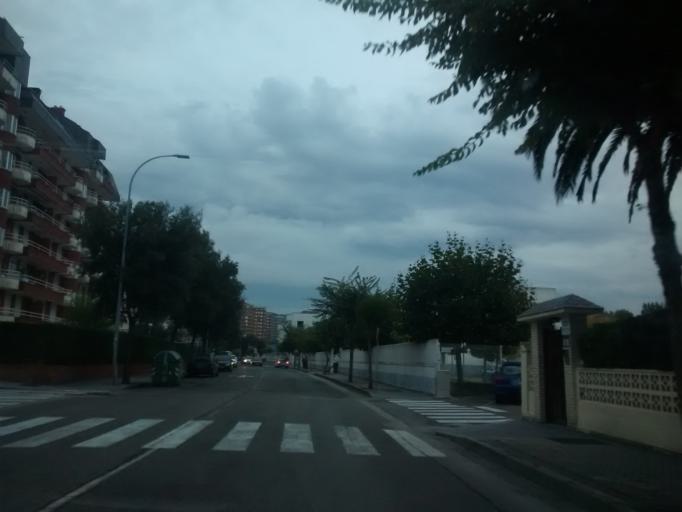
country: ES
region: Cantabria
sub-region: Provincia de Cantabria
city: Colindres
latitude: 43.4153
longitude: -3.4425
